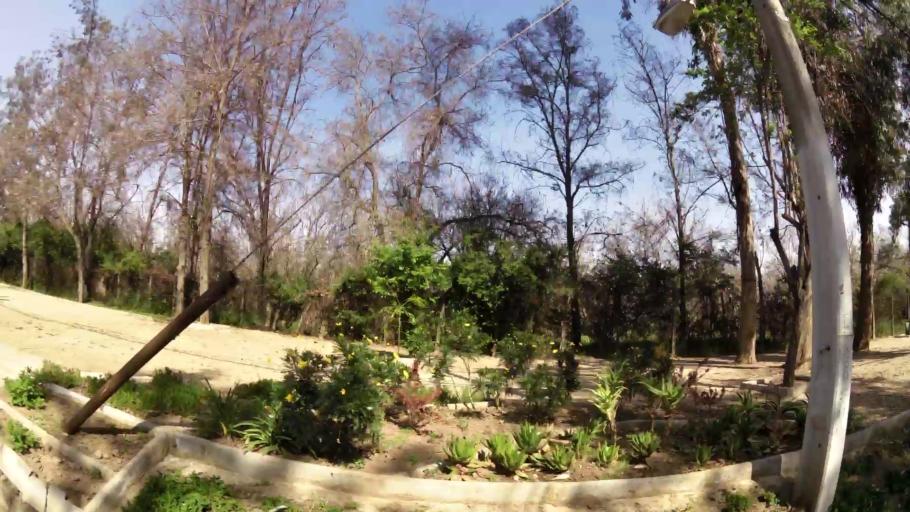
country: CL
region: Santiago Metropolitan
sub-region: Provincia de Santiago
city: Villa Presidente Frei, Nunoa, Santiago, Chile
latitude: -33.5288
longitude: -70.5711
